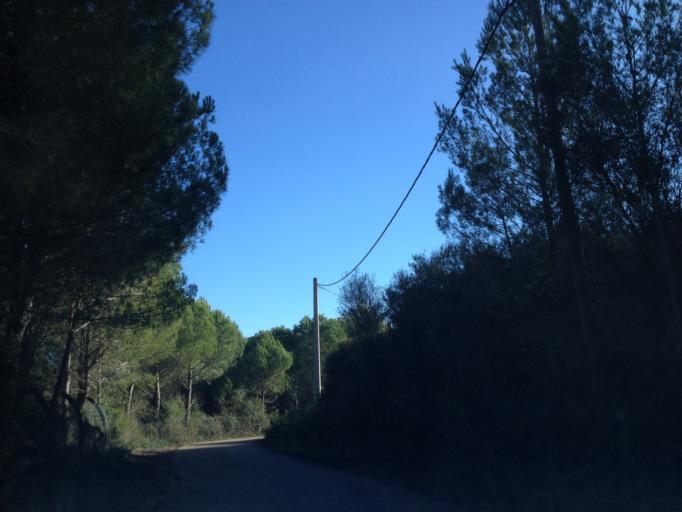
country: ES
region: Balearic Islands
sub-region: Illes Balears
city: Sineu
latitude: 39.6526
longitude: 3.0365
